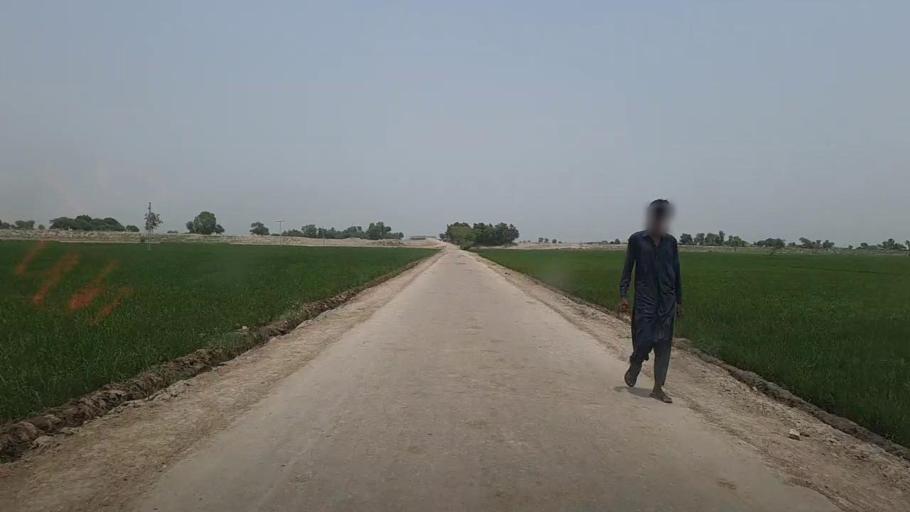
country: PK
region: Sindh
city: Sita Road
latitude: 27.0478
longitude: 67.8472
